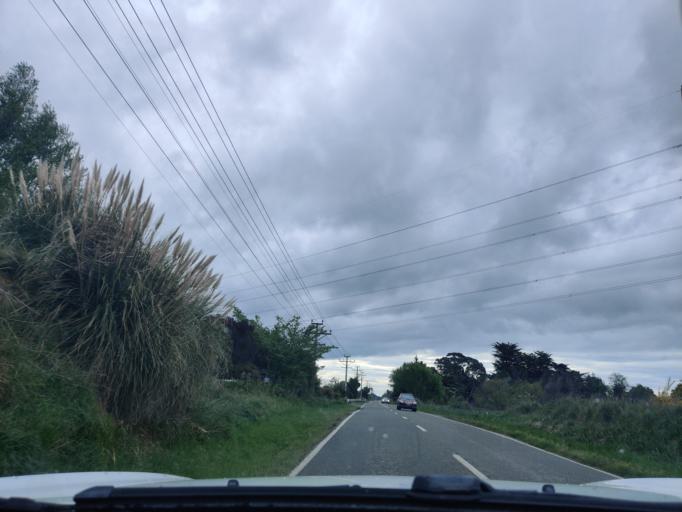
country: NZ
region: Manawatu-Wanganui
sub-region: Palmerston North City
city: Palmerston North
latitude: -40.3434
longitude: 175.7124
